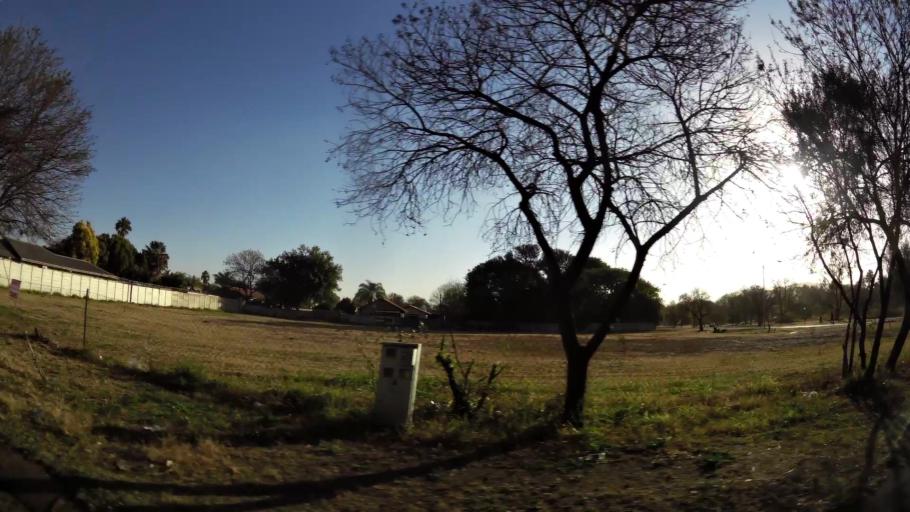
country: ZA
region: Gauteng
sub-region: City of Tshwane Metropolitan Municipality
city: Pretoria
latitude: -25.7092
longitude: 28.2055
